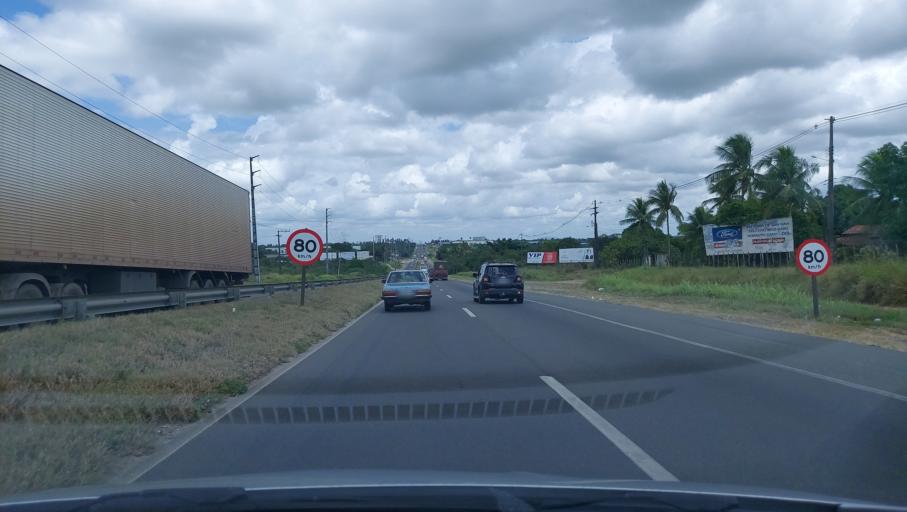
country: BR
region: Bahia
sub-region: Conceicao Do Jacuipe
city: Conceicao do Jacuipe
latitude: -12.3287
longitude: -38.8606
